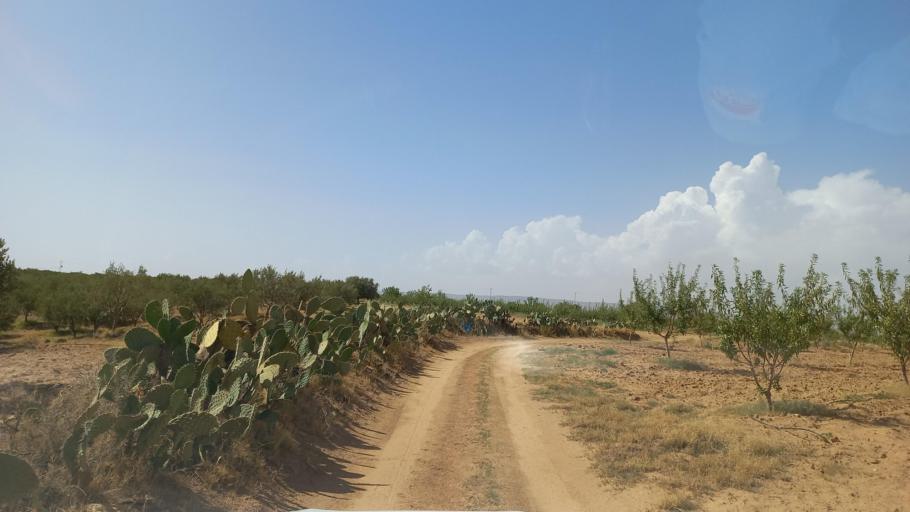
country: TN
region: Al Qasrayn
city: Kasserine
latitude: 35.2118
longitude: 9.0338
